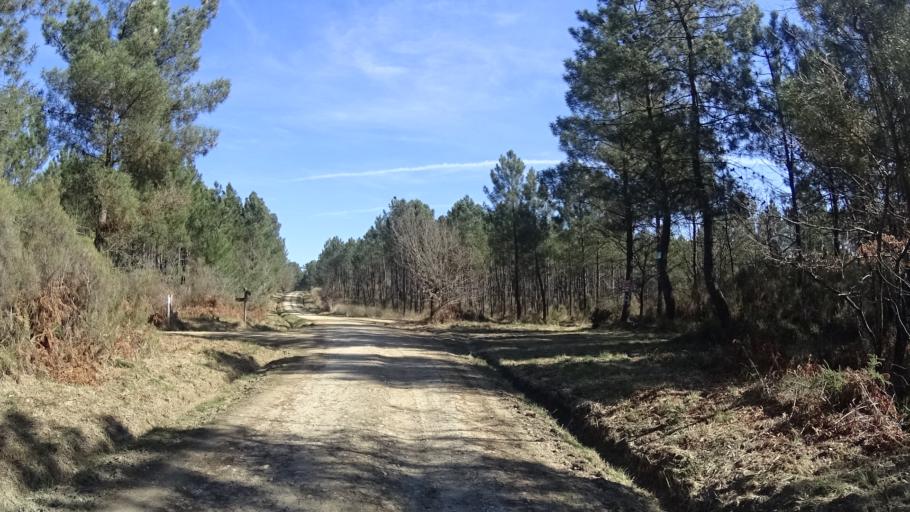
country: FR
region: Aquitaine
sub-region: Departement de la Dordogne
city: Riberac
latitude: 45.1875
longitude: 0.3113
